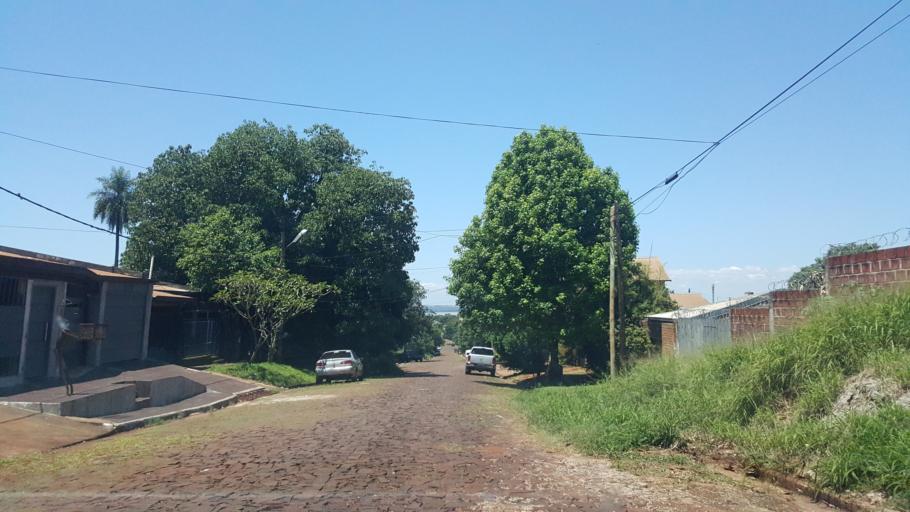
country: AR
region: Misiones
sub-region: Departamento de Capital
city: Posadas
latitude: -27.3913
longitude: -55.9119
